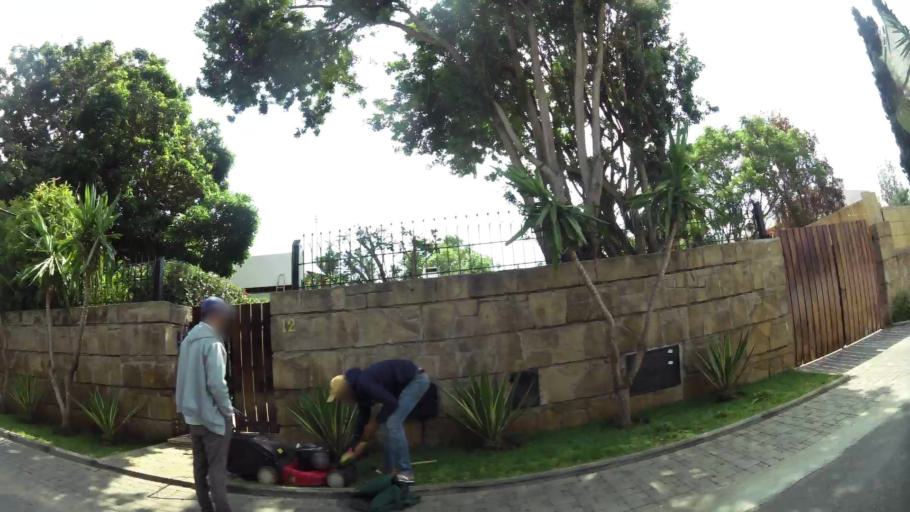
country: MA
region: Rabat-Sale-Zemmour-Zaer
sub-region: Rabat
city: Rabat
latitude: 33.9825
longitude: -6.8381
